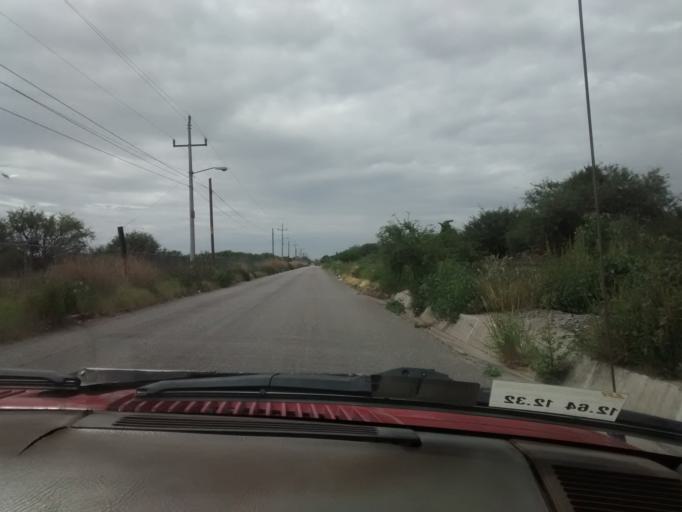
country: MX
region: Puebla
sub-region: Santiago Miahuatlan
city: San Jose Monte Chiquito
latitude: 18.4978
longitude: -97.4232
